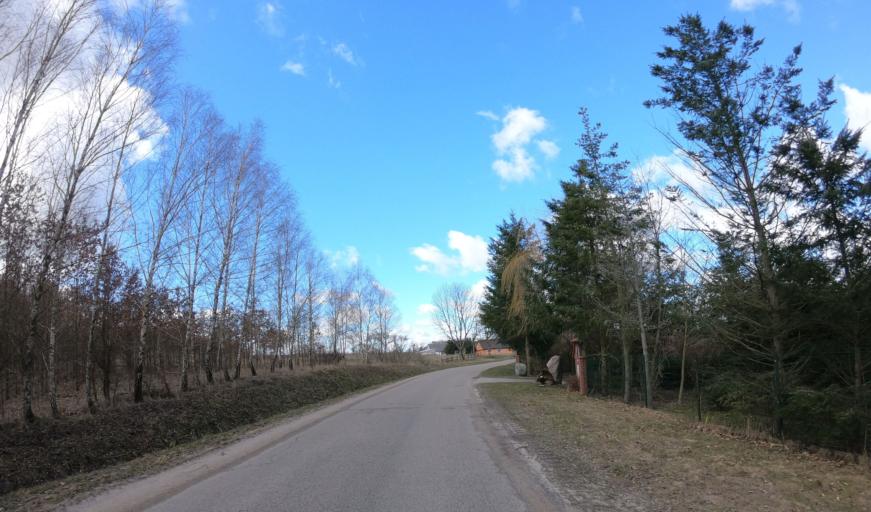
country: PL
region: West Pomeranian Voivodeship
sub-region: Powiat drawski
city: Zlocieniec
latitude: 53.4833
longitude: 15.9130
